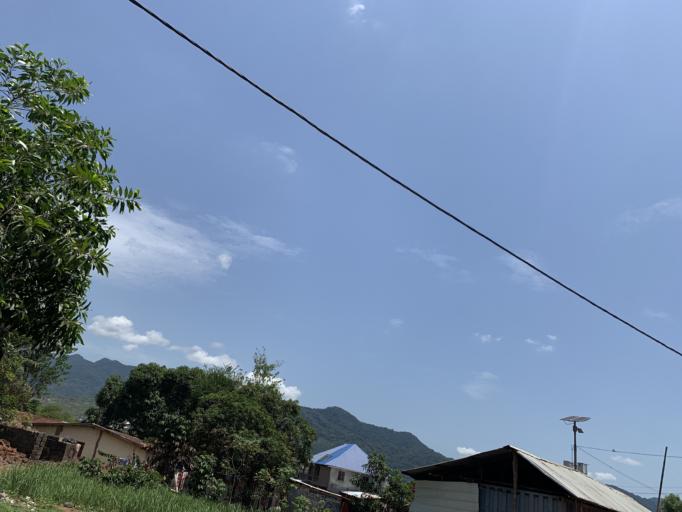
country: SL
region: Western Area
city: Waterloo
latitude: 8.3148
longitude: -13.0728
